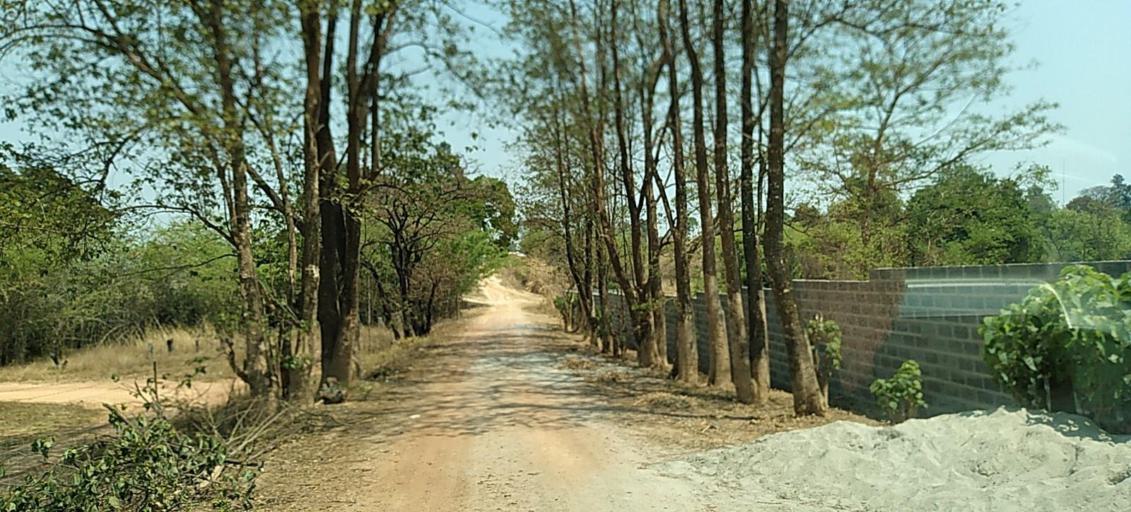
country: ZM
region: Copperbelt
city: Chambishi
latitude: -12.6293
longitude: 27.9422
